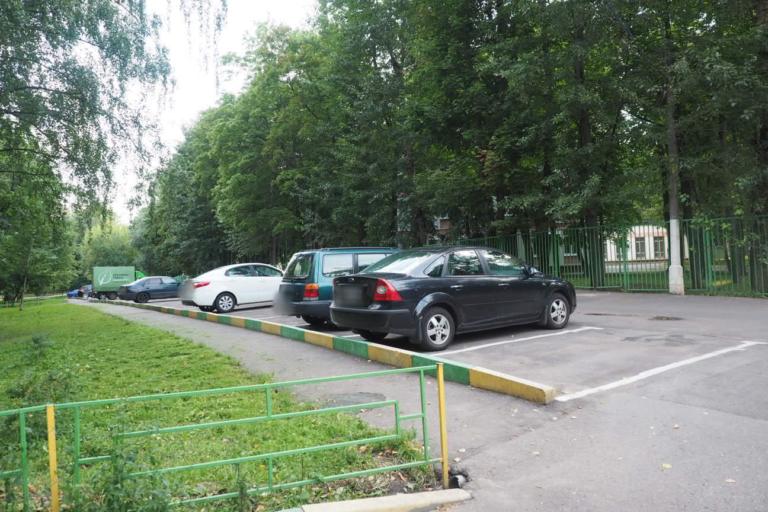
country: RU
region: Moskovskaya
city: Cheremushki
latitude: 55.6703
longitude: 37.5752
